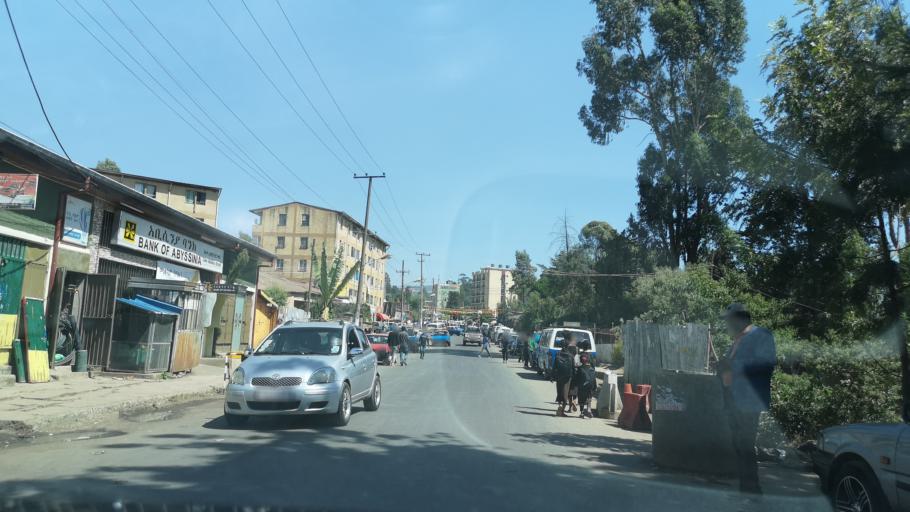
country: ET
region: Adis Abeba
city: Addis Ababa
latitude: 9.0512
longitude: 38.7489
